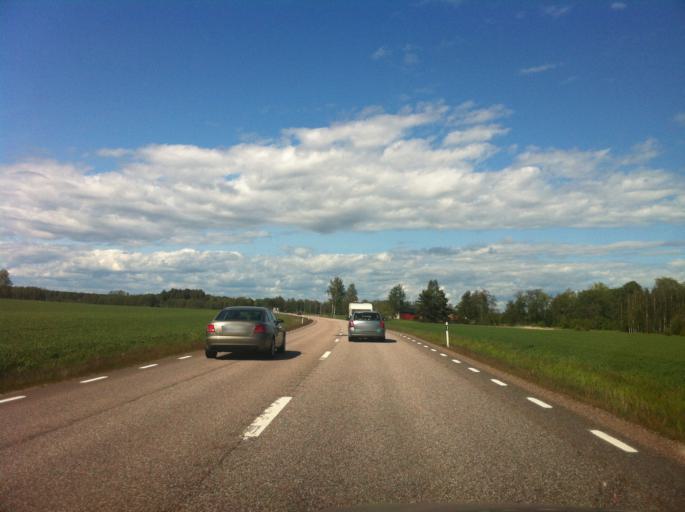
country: SE
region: Vaestra Goetaland
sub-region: Gullspangs Kommun
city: Gullspang
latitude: 59.1146
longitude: 14.1764
